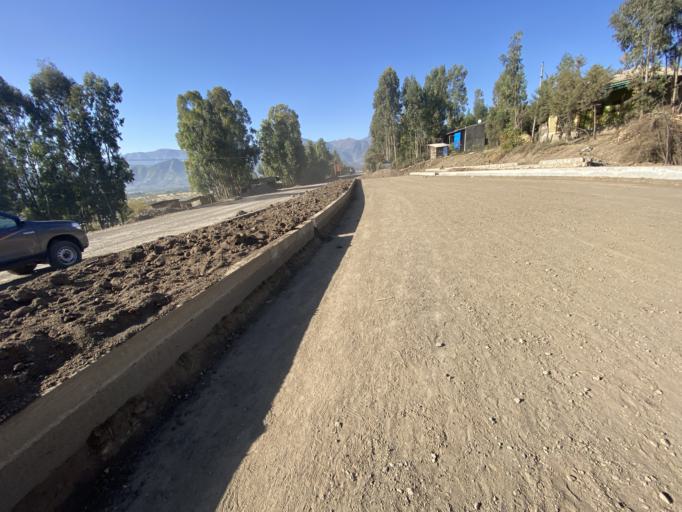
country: ET
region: Amhara
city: Robit
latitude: 11.8275
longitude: 39.5677
